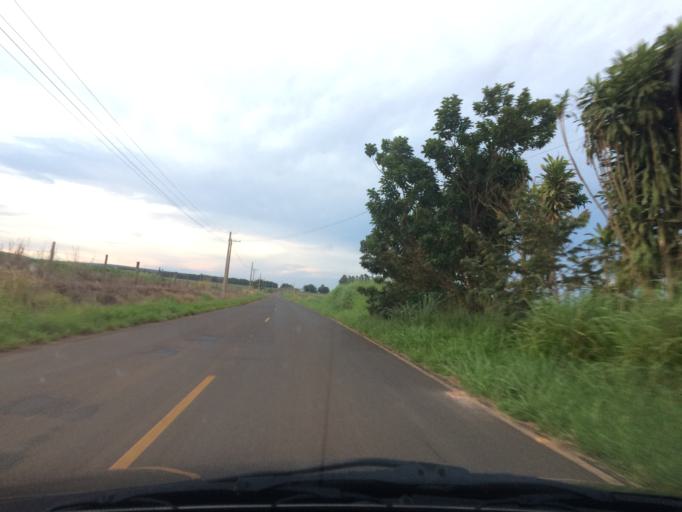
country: BR
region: Sao Paulo
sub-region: Casa Branca
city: Casa Branca
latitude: -21.7463
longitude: -47.1698
